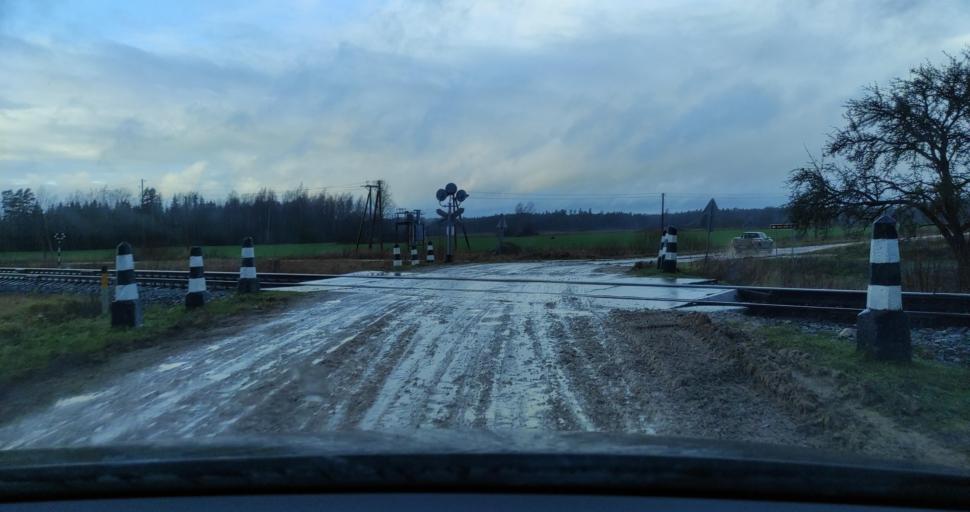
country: LV
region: Skrunda
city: Skrunda
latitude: 56.7108
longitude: 22.2011
